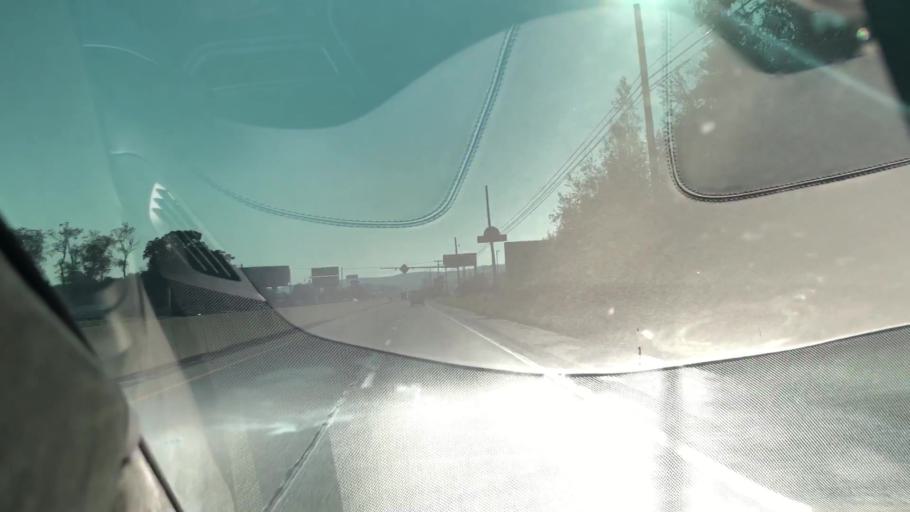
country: US
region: Pennsylvania
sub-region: Indiana County
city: Blairsville
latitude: 40.4415
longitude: -79.2410
